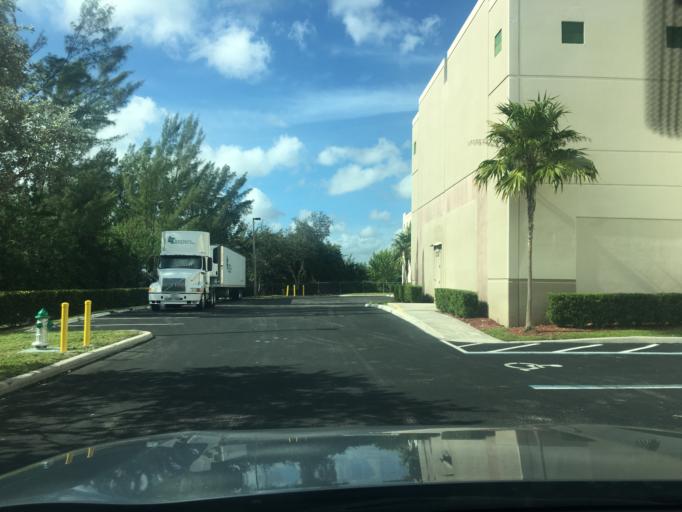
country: US
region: Florida
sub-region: Broward County
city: Broadview Park
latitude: 26.0754
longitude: -80.1839
